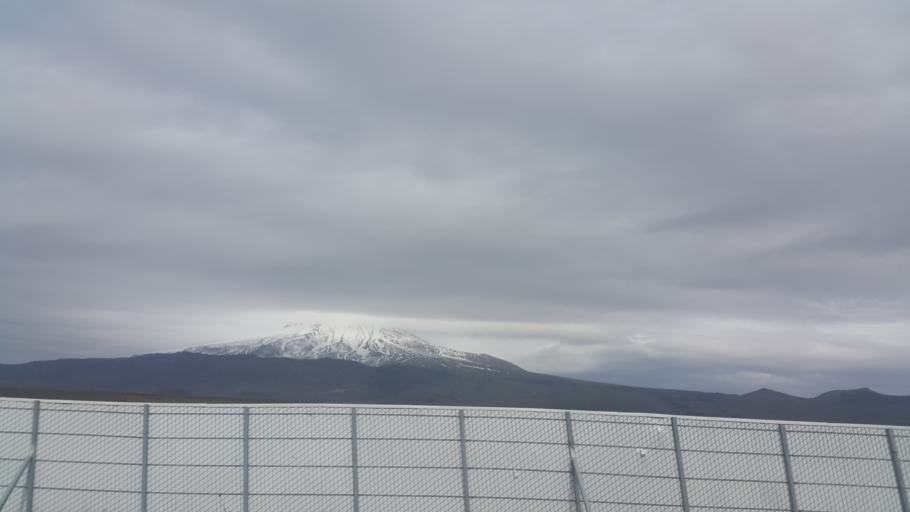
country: TR
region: Aksaray
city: Taspinar
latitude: 38.1115
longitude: 34.0338
